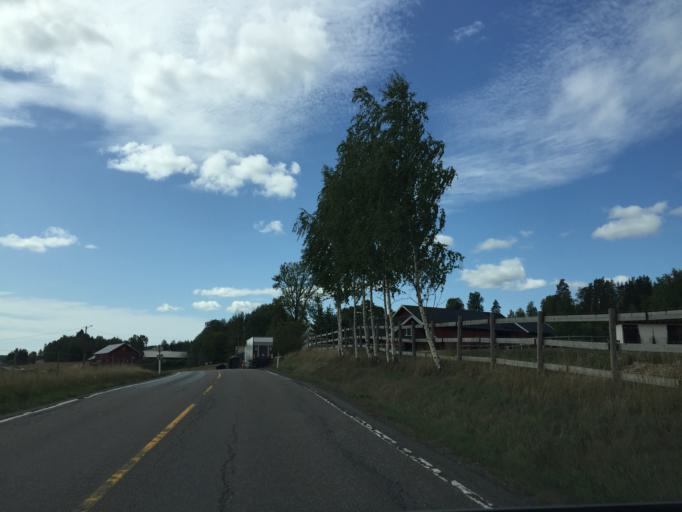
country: NO
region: Ostfold
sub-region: Hobol
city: Elvestad
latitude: 59.6080
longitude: 10.9182
